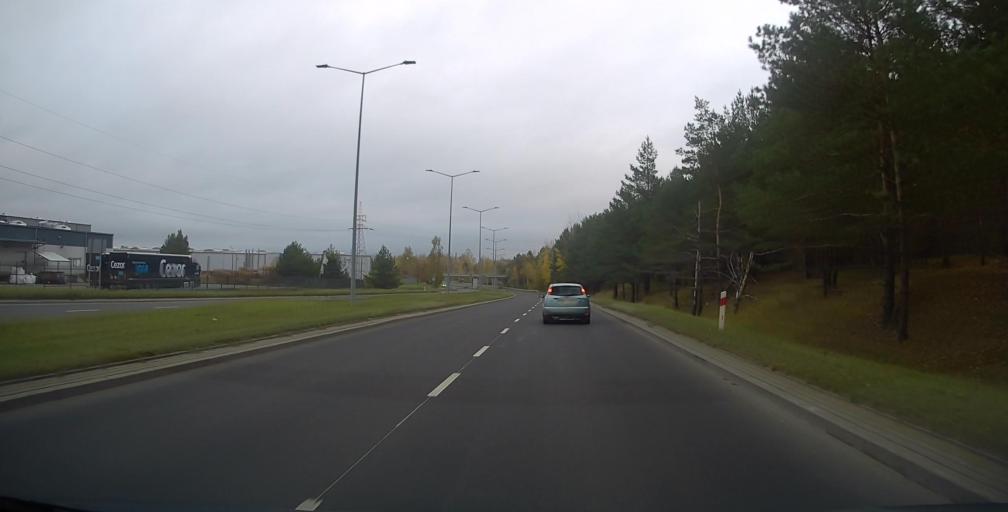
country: PL
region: Warmian-Masurian Voivodeship
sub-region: Powiat elcki
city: Elk
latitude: 53.8156
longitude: 22.3852
